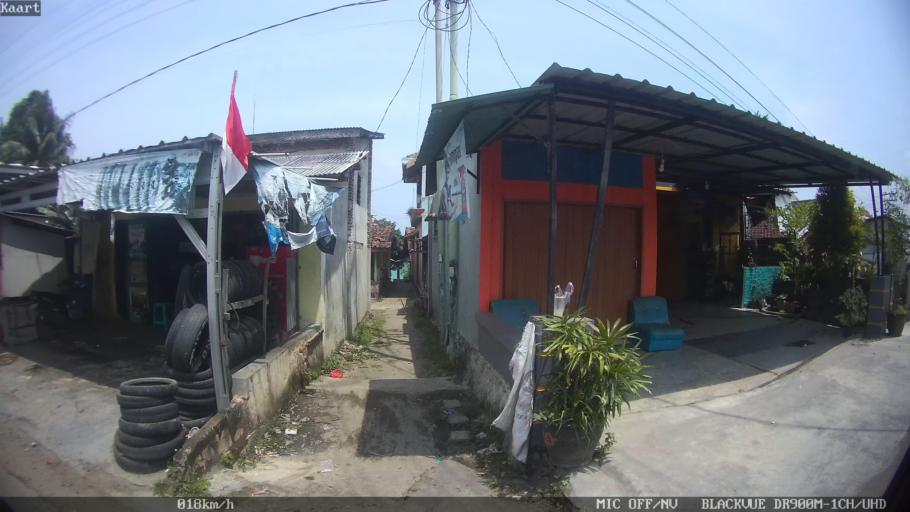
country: ID
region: Lampung
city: Bandarlampung
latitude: -5.4458
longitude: 105.2536
